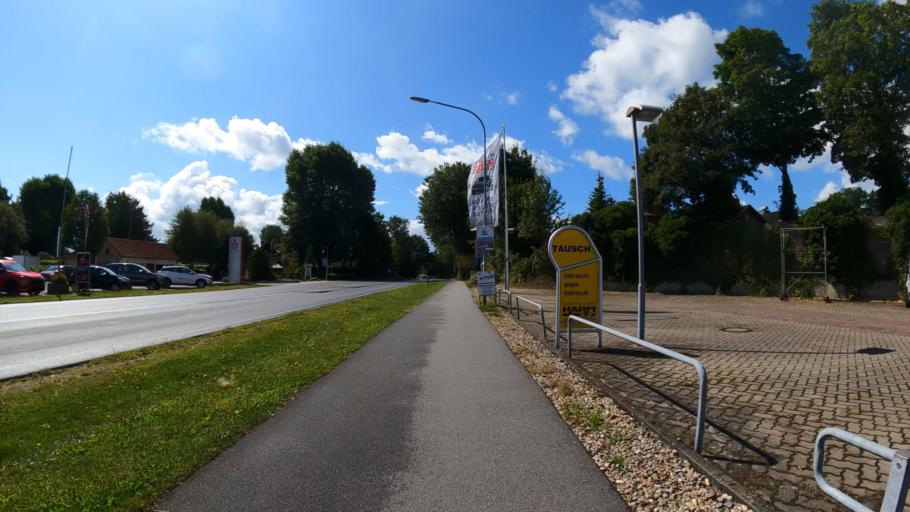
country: DE
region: Schleswig-Holstein
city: Bad Bramstedt
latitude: 53.9292
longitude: 9.8895
